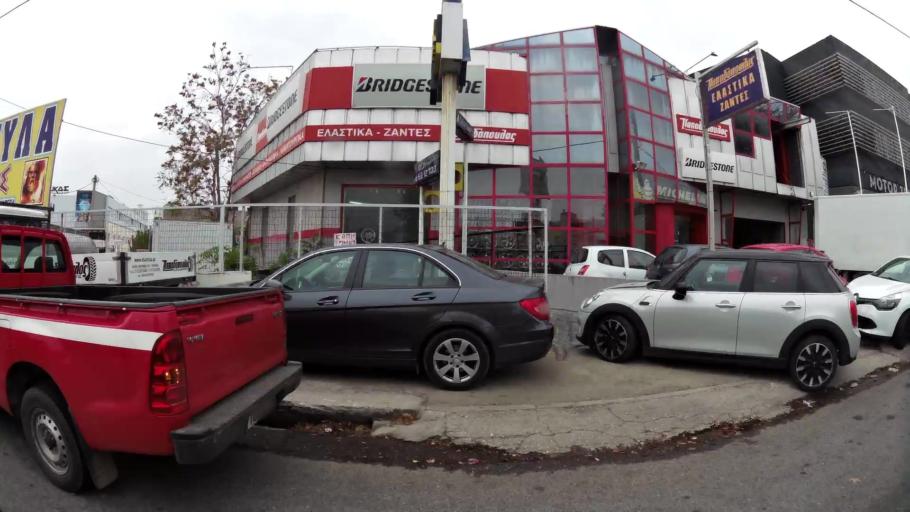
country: GR
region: Attica
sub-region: Nomarchia Athinas
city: Aigaleo
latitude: 37.9976
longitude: 23.6920
